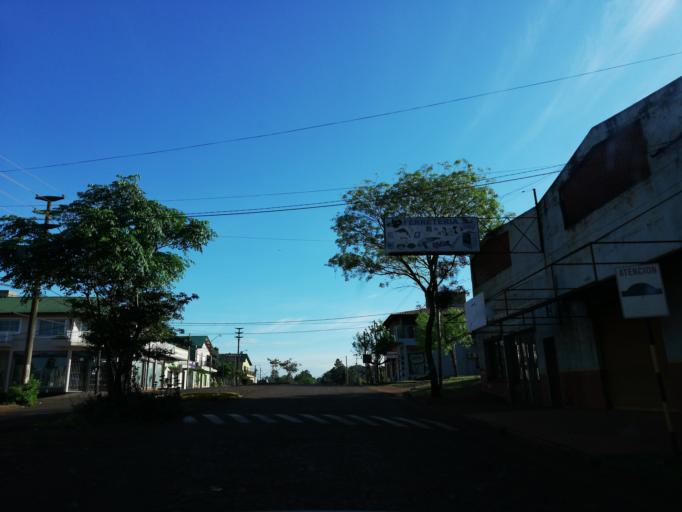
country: AR
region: Misiones
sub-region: Departamento de Obera
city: Obera
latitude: -27.5005
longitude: -55.1186
